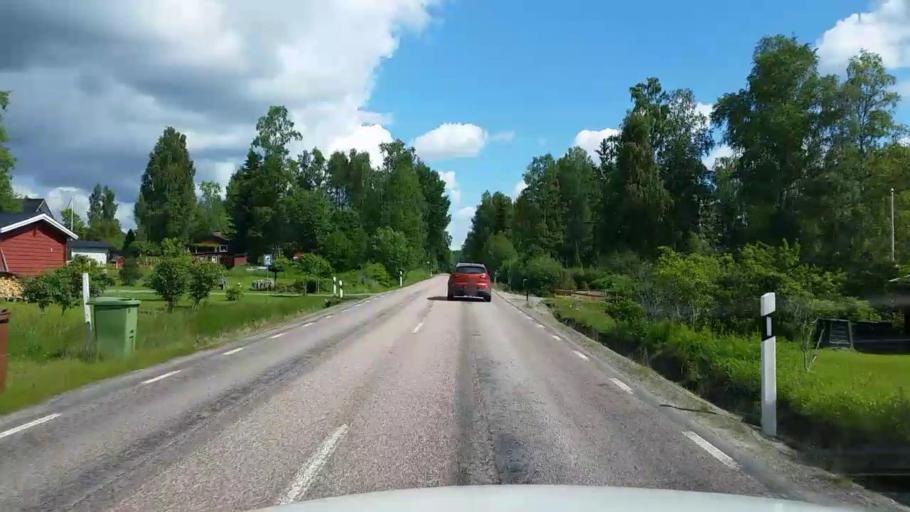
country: SE
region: Vaestmanland
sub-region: Skinnskattebergs Kommun
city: Skinnskatteberg
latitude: 59.7569
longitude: 15.8182
